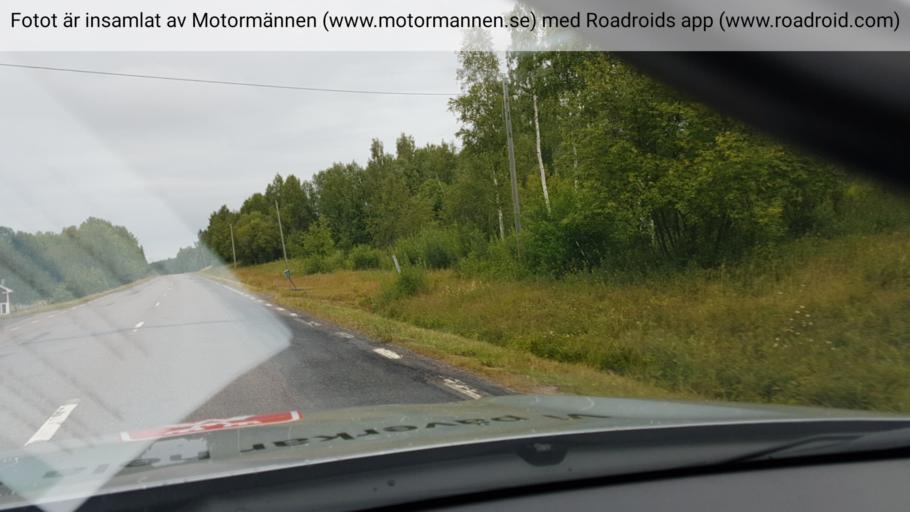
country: SE
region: Norrbotten
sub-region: Alvsbyns Kommun
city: AElvsbyn
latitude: 66.1553
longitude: 20.8774
